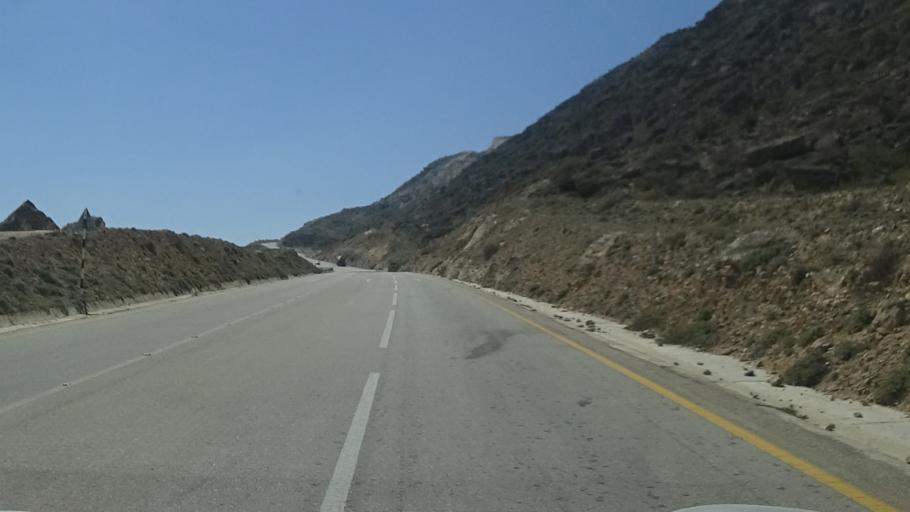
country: OM
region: Zufar
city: Salalah
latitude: 16.8342
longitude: 53.6754
